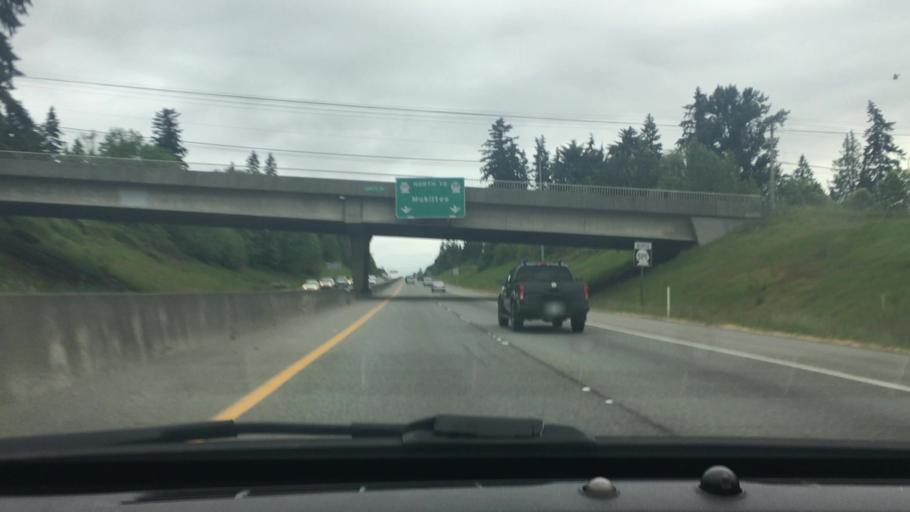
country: US
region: Washington
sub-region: Snohomish County
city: Alderwood Manor
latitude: 47.8494
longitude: -122.2743
